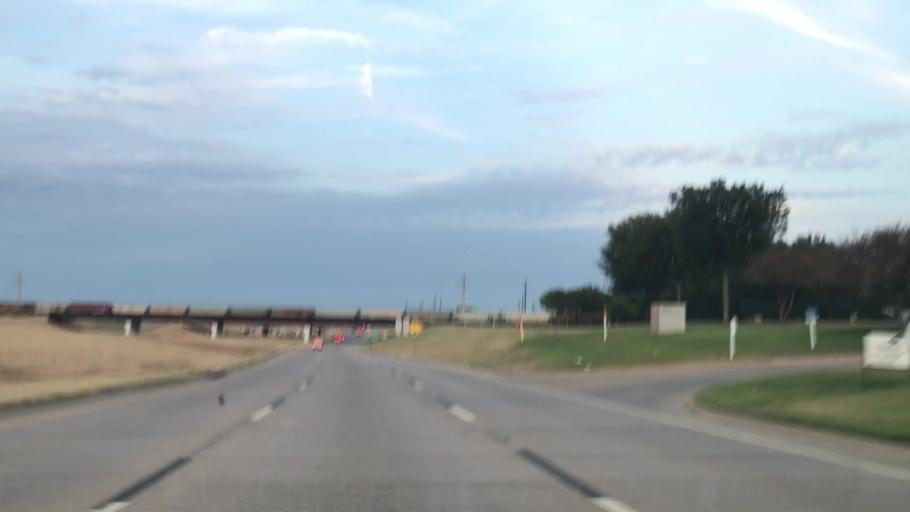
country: US
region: Texas
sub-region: Denton County
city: Roanoke
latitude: 32.9852
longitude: -97.2419
